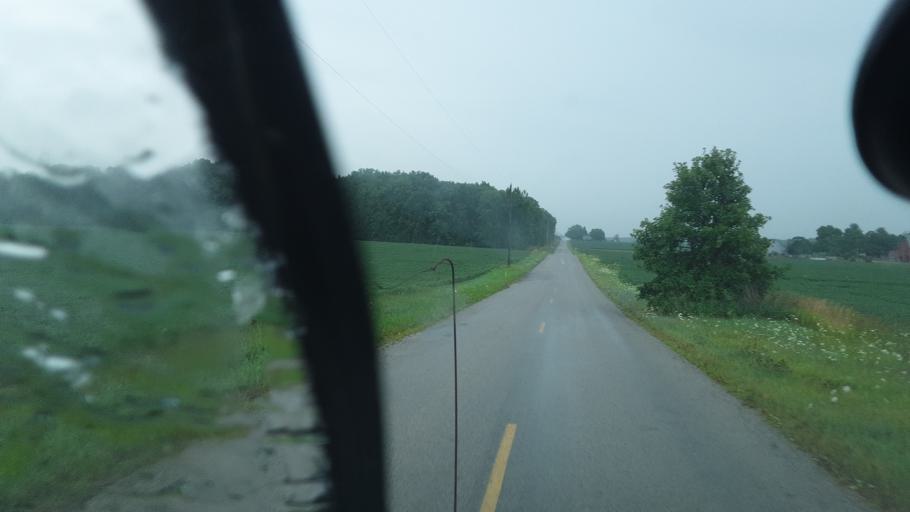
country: US
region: Indiana
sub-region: DeKalb County
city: Butler
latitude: 41.4583
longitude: -84.8139
